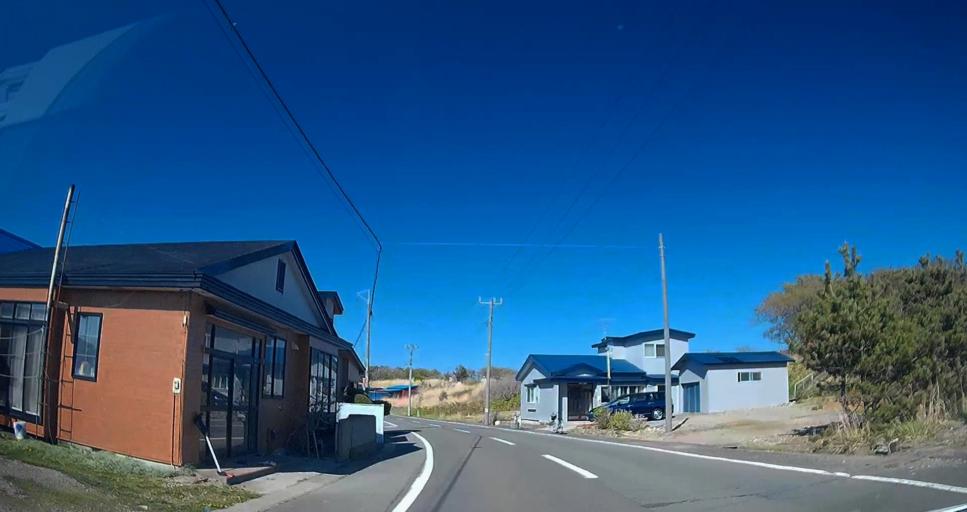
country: JP
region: Hokkaido
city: Hakodate
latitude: 41.5407
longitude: 140.9118
